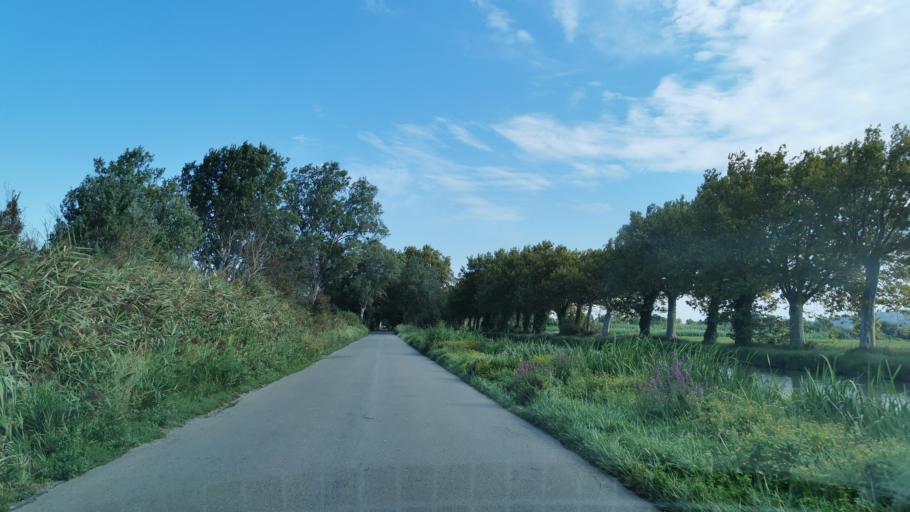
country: FR
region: Languedoc-Roussillon
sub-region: Departement de l'Aude
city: Gruissan
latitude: 43.1245
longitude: 3.0310
